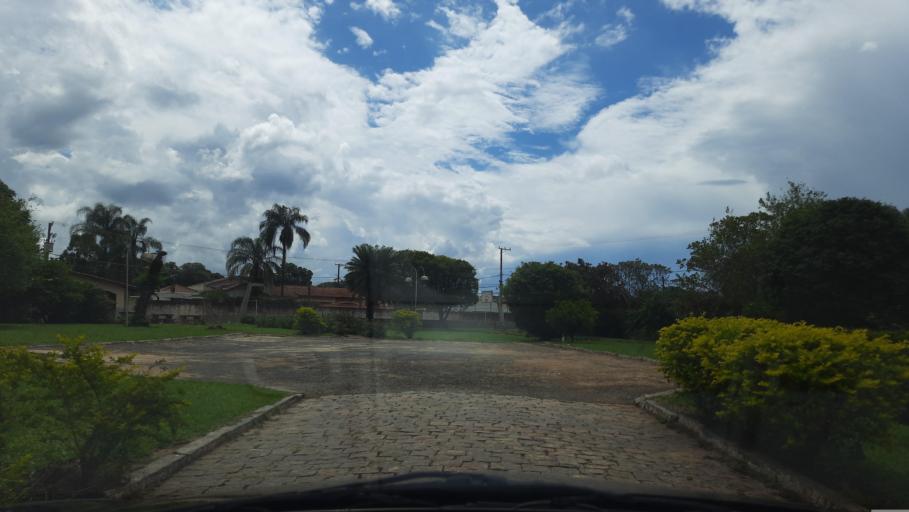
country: BR
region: Sao Paulo
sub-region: Casa Branca
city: Casa Branca
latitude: -21.7827
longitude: -47.0636
